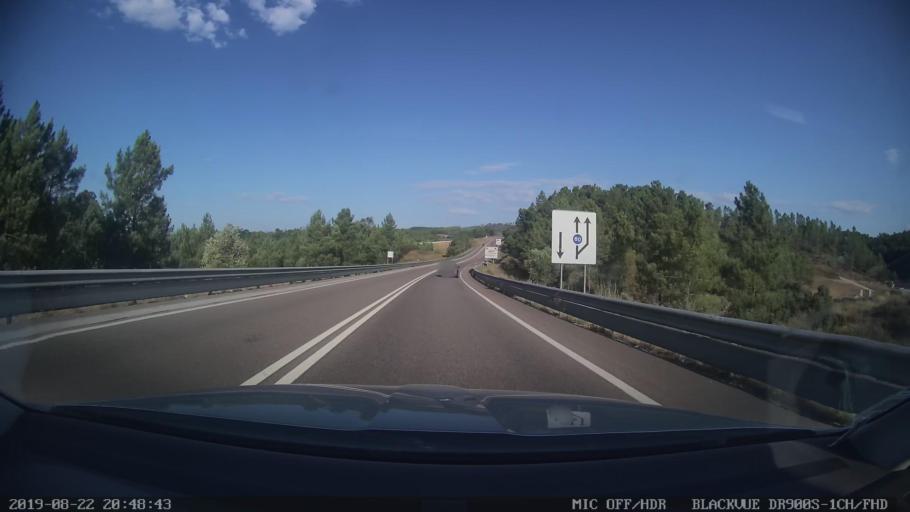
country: PT
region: Castelo Branco
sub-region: Proenca-A-Nova
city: Proenca-a-Nova
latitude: 39.7359
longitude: -7.9161
